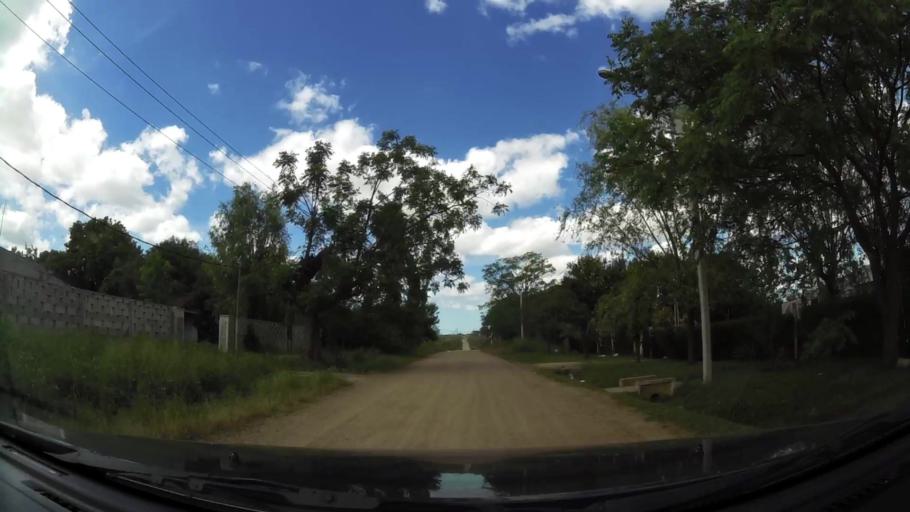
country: UY
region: Canelones
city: Colonia Nicolich
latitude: -34.8143
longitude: -56.0452
